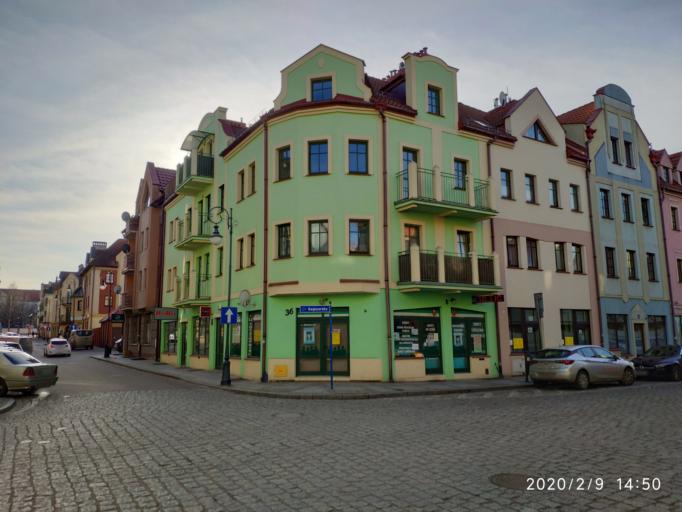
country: PL
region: Lower Silesian Voivodeship
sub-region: Powiat glogowski
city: Glogow
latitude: 51.6645
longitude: 16.0914
